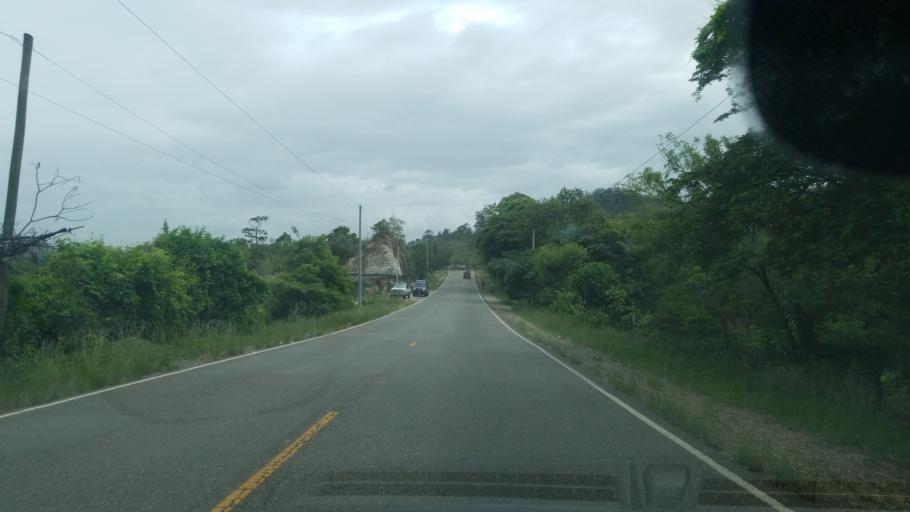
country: HN
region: Ocotepeque
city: Lucerna
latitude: 14.5800
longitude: -88.9295
